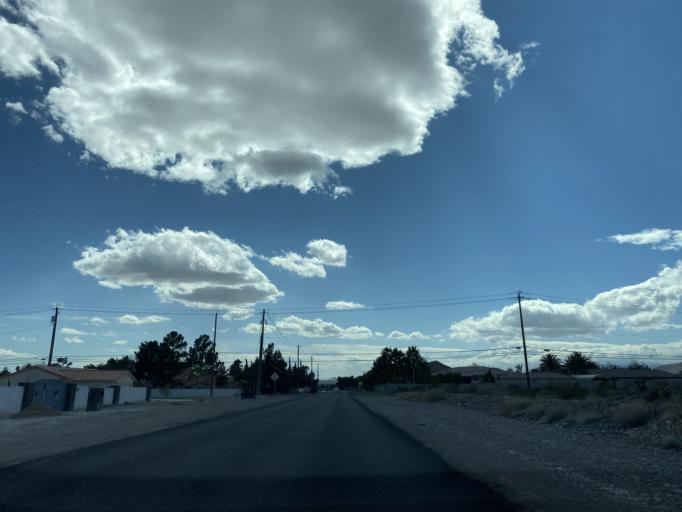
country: US
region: Nevada
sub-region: Clark County
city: Summerlin South
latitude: 36.2657
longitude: -115.2884
